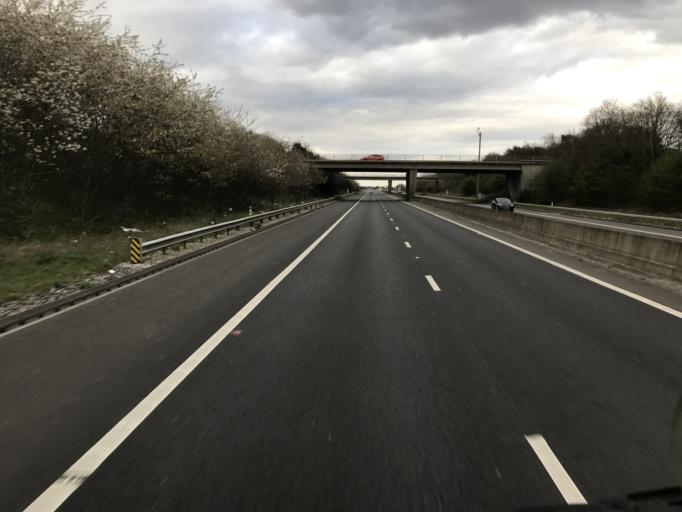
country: GB
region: England
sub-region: Doncaster
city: Armthorpe
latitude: 53.5384
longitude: -1.0233
